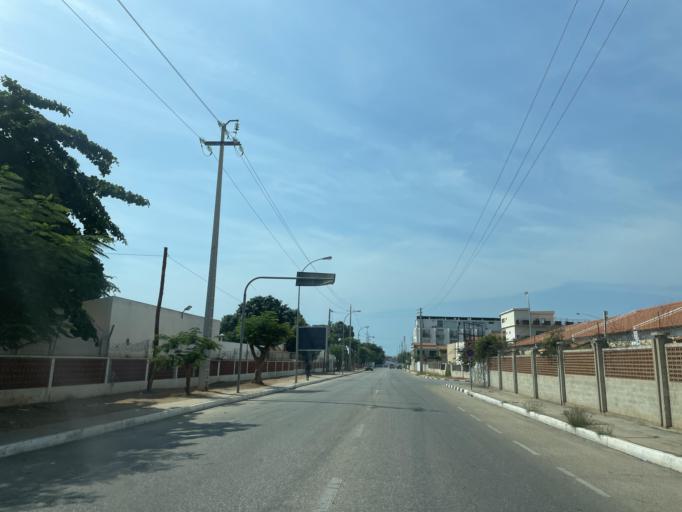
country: AO
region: Luanda
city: Luanda
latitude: -8.9113
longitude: 13.1831
